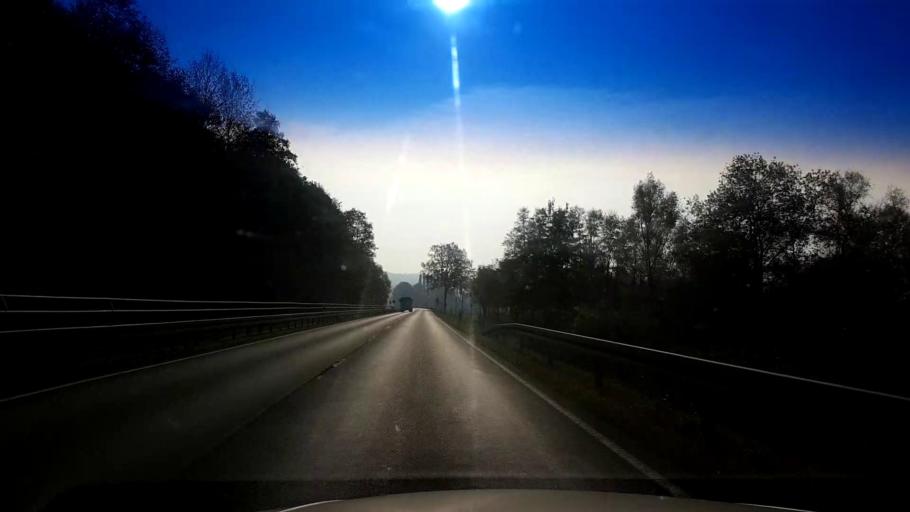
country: DE
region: Bavaria
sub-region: Upper Franconia
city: Neuenmarkt
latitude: 50.1094
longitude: 11.5906
